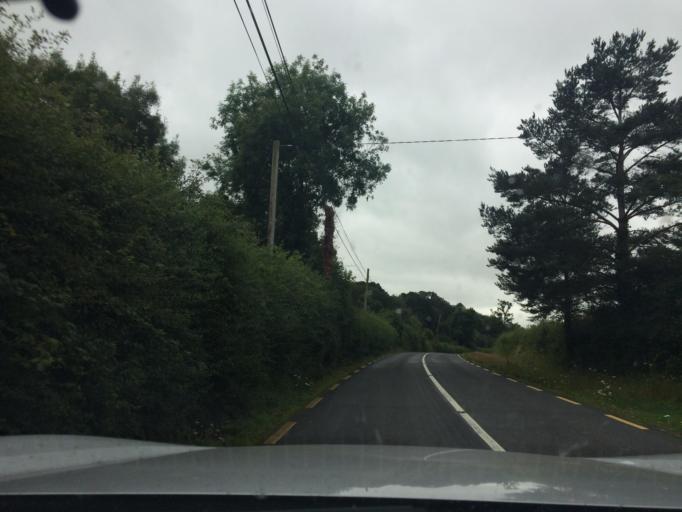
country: IE
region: Munster
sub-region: South Tipperary
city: Cluain Meala
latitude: 52.3290
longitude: -7.7327
